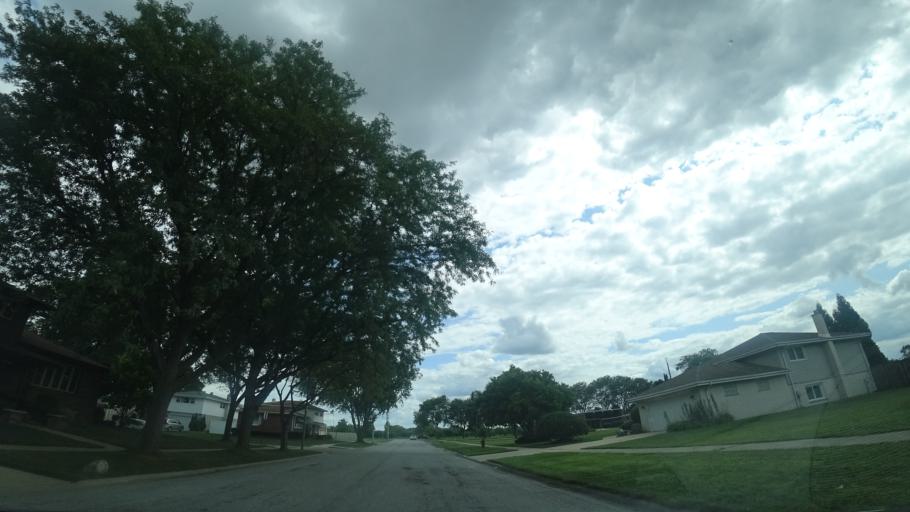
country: US
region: Illinois
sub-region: Cook County
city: Alsip
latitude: 41.6925
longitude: -87.7349
